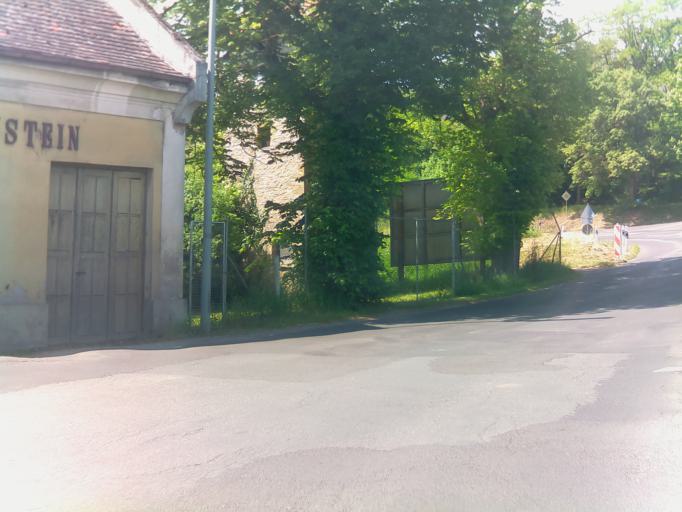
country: DE
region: Bavaria
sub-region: Regierungsbezirk Unterfranken
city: Arnstein
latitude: 49.9783
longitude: 9.9615
